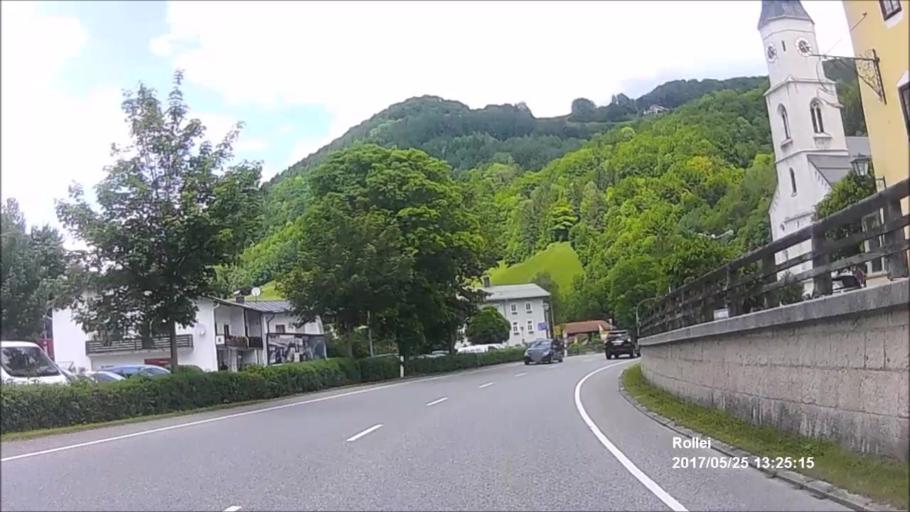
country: DE
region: Bavaria
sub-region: Upper Bavaria
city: Marktschellenberg
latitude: 47.6944
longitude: 13.0459
